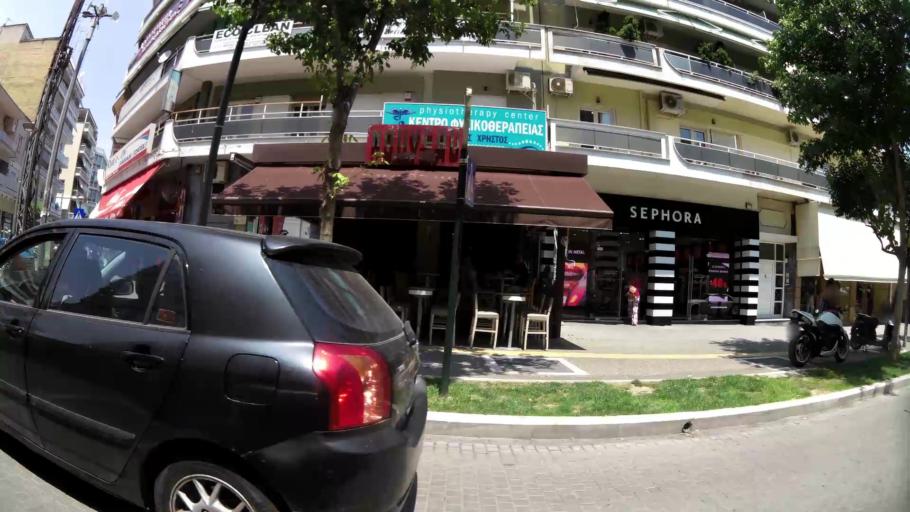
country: GR
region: Central Macedonia
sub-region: Nomos Imathias
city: Veroia
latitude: 40.5237
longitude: 22.2054
